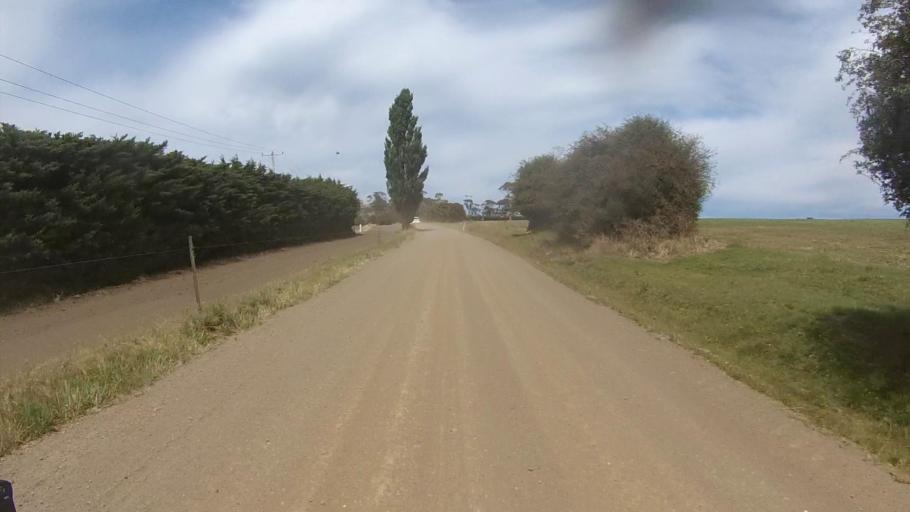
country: AU
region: Tasmania
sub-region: Sorell
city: Sorell
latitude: -42.8161
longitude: 147.8259
